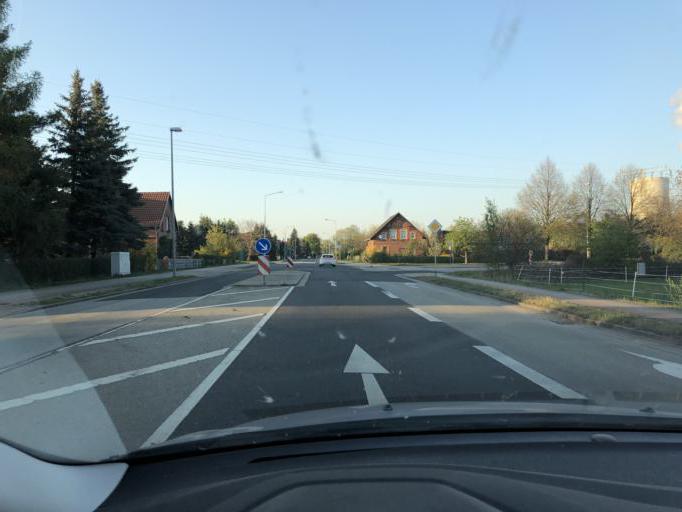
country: DE
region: Brandenburg
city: Spremberg
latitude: 51.5311
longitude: 14.3389
